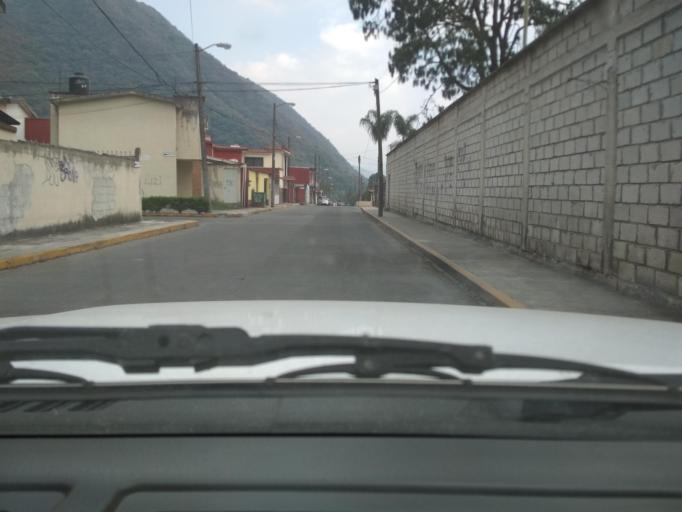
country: MX
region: Veracruz
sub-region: Mariano Escobedo
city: Palmira
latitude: 18.8735
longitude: -97.0977
